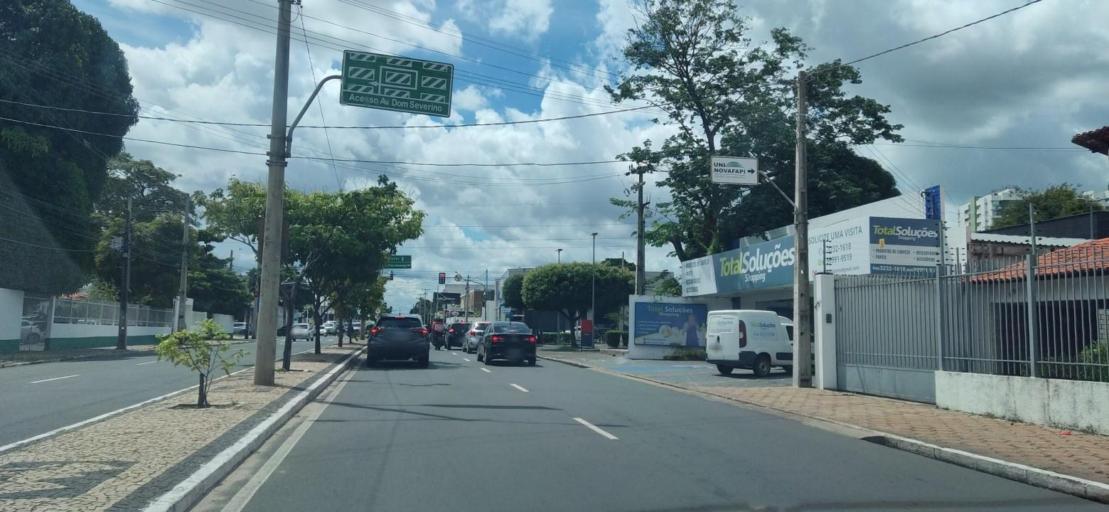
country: BR
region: Piaui
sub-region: Teresina
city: Teresina
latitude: -5.0707
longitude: -42.7923
